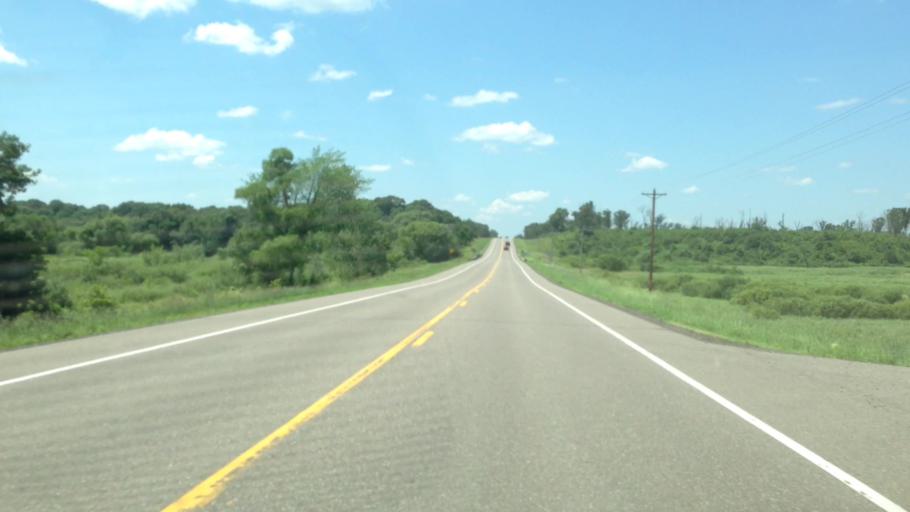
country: US
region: Minnesota
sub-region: Sherburne County
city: Zimmerman
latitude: 45.4438
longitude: -93.6517
